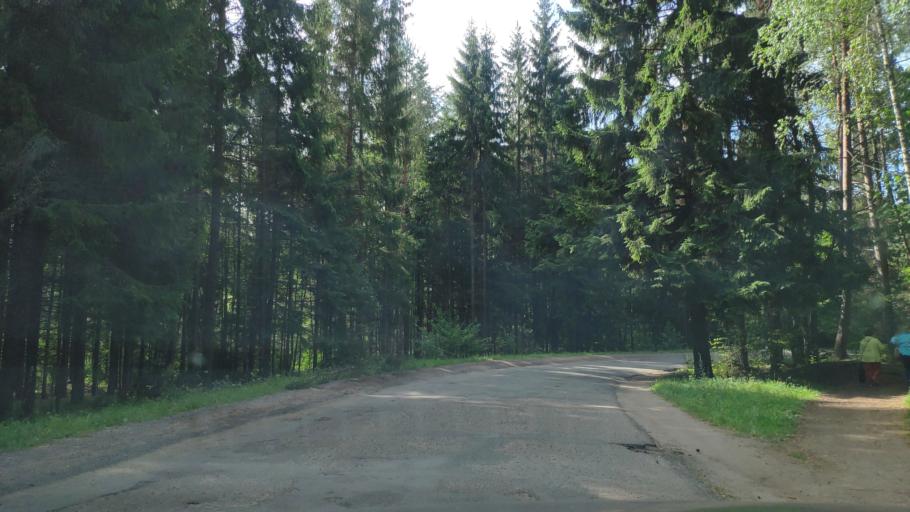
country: BY
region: Minsk
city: Zaslawye
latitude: 53.9755
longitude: 27.2909
